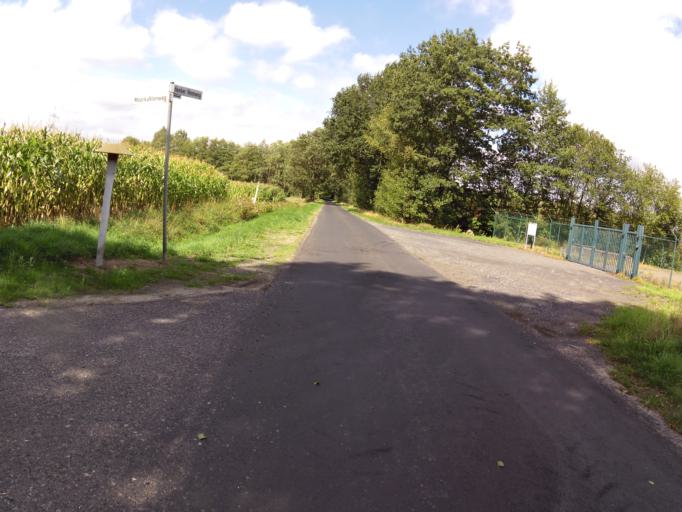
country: DE
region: North Rhine-Westphalia
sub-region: Regierungsbezirk Munster
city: Gronau
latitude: 52.1654
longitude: 7.0094
